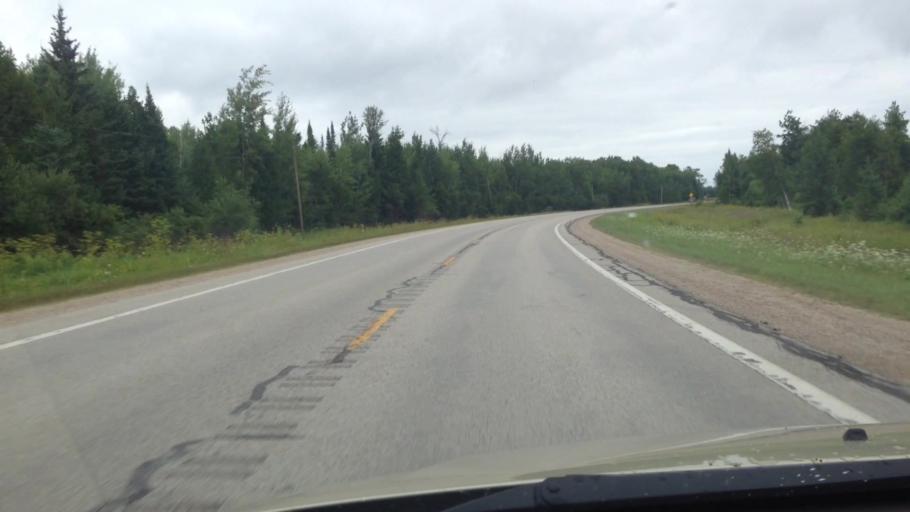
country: US
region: Michigan
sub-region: Delta County
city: Escanaba
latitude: 45.5550
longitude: -87.2683
